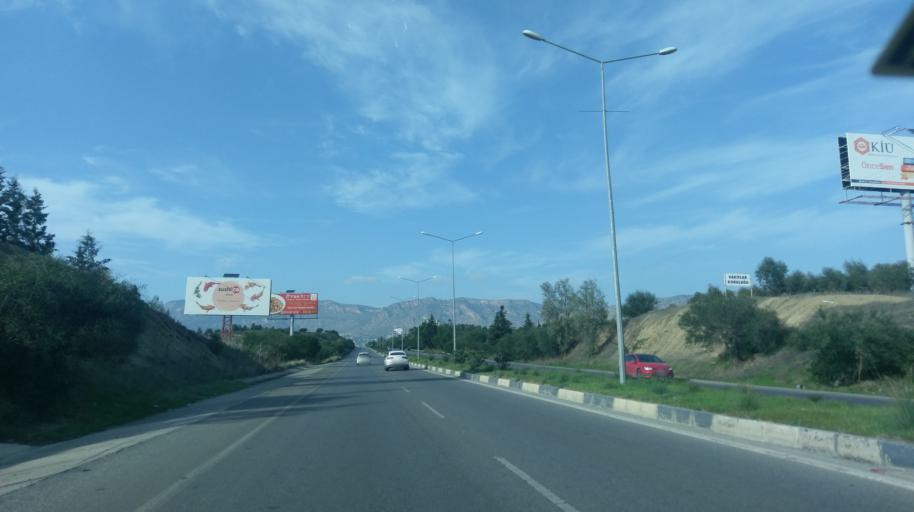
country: CY
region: Lefkosia
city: Nicosia
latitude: 35.2429
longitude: 33.3087
